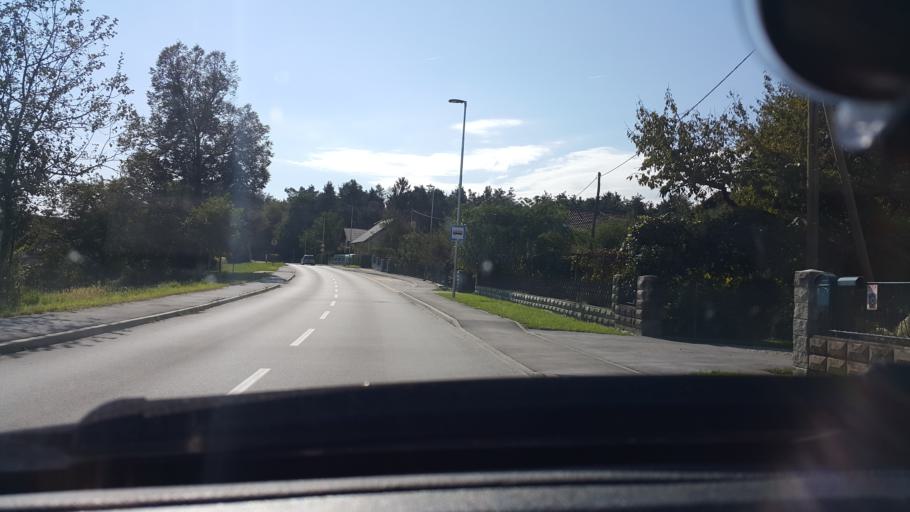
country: SI
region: Miklavz na Dravskem Polju
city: Miklavz na Dravskem Polju
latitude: 46.4763
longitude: 15.7062
